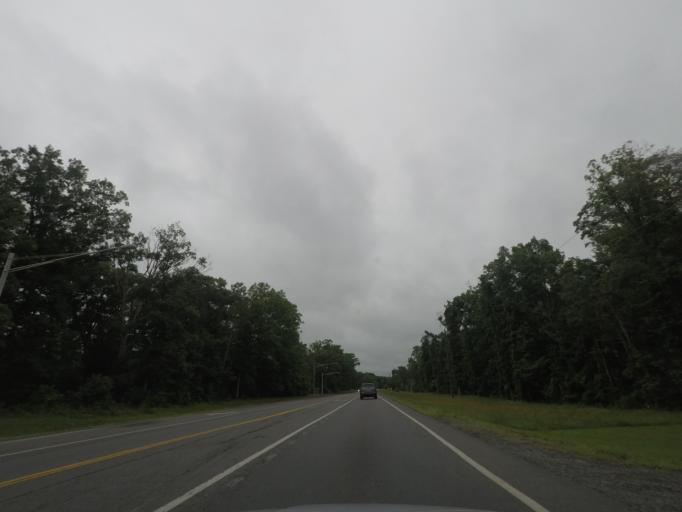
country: US
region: Virginia
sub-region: Prince William County
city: Haymarket
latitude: 38.7929
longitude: -77.6649
